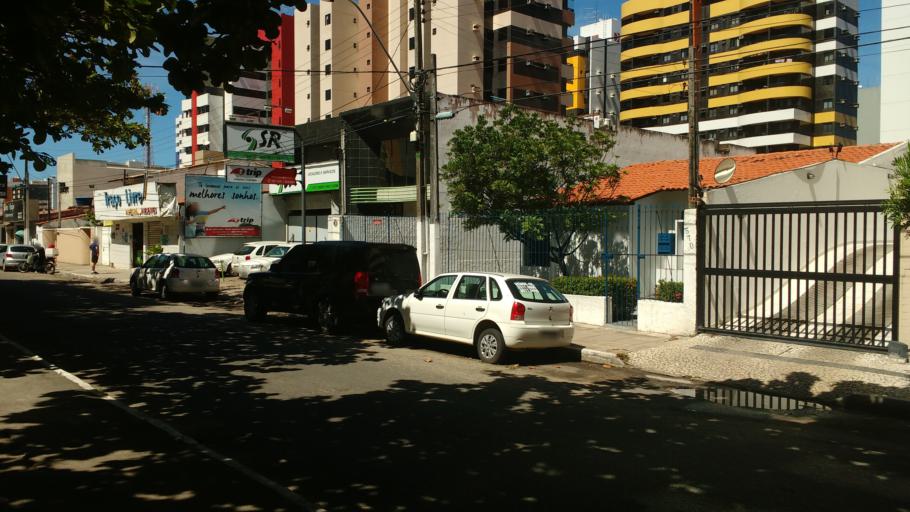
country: BR
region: Alagoas
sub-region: Maceio
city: Maceio
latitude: -9.6588
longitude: -35.7056
